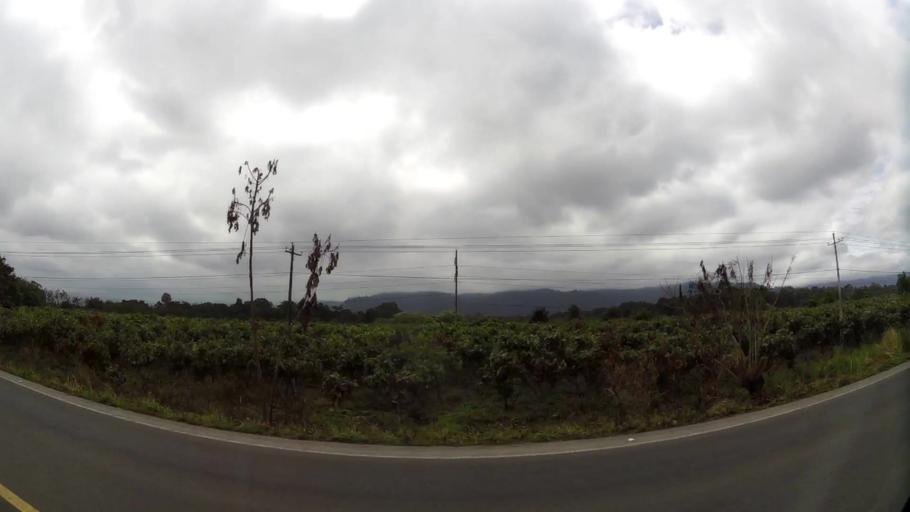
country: EC
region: Guayas
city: Naranjal
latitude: -2.6944
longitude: -79.6449
